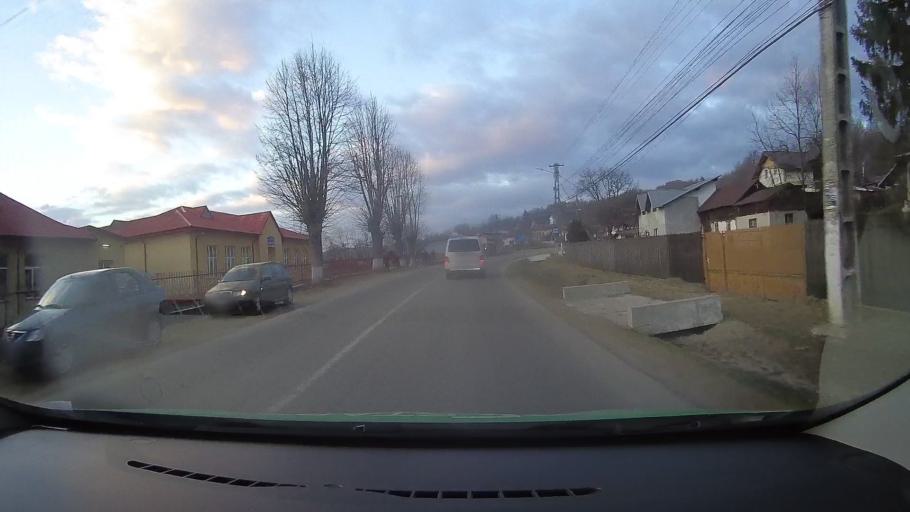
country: RO
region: Dambovita
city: Iedera de Jos
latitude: 45.0253
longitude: 25.6353
